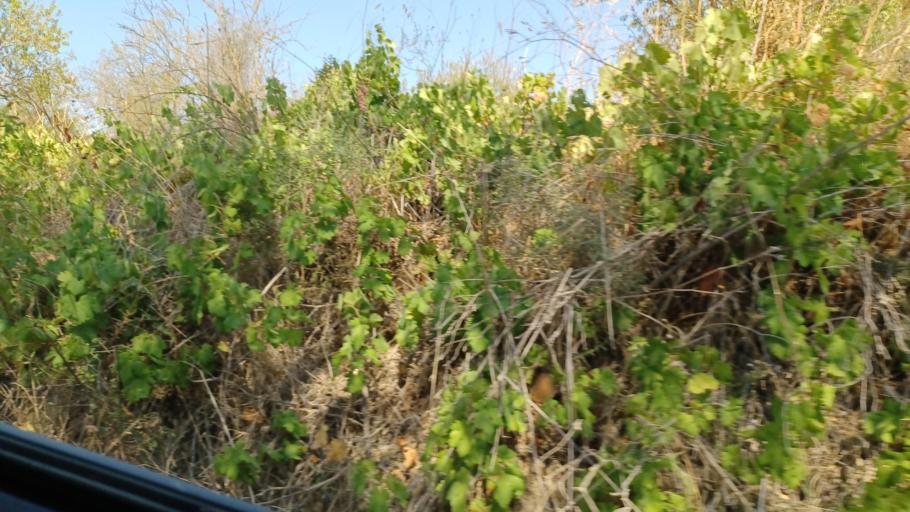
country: CY
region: Pafos
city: Tala
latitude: 34.9183
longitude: 32.4780
